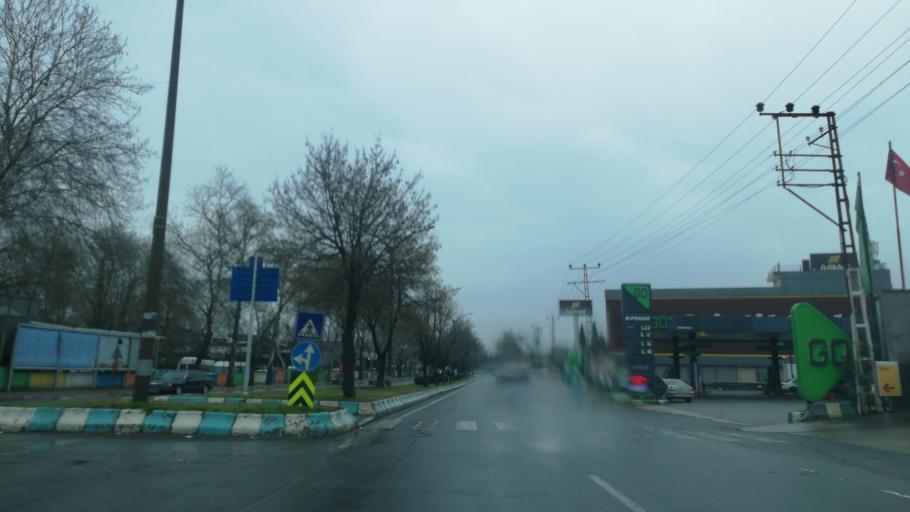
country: TR
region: Kahramanmaras
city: Kahramanmaras
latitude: 37.5645
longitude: 36.9516
